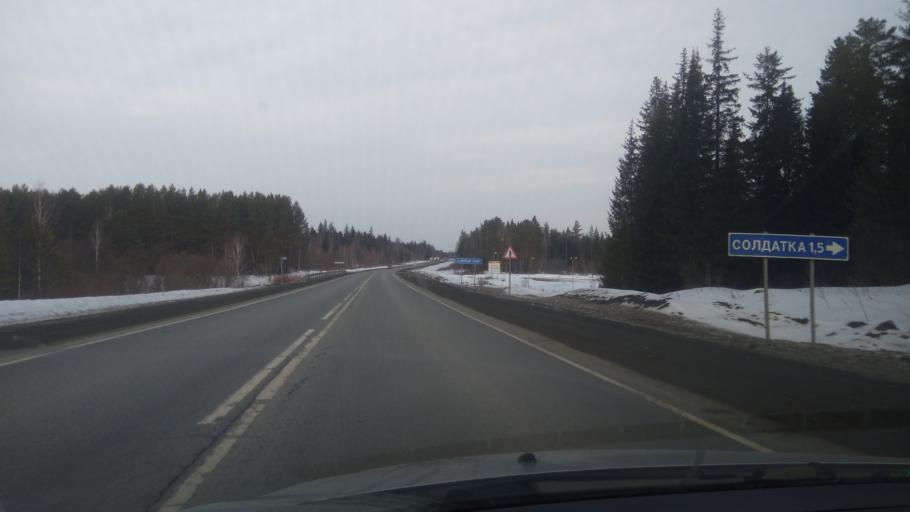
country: RU
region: Sverdlovsk
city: Atig
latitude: 56.8031
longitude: 59.3778
